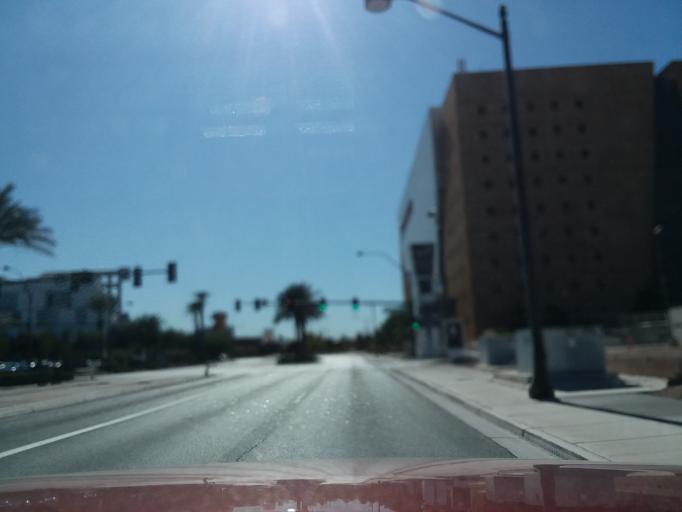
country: US
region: Nevada
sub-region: Clark County
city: Las Vegas
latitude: 36.1690
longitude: -115.1547
